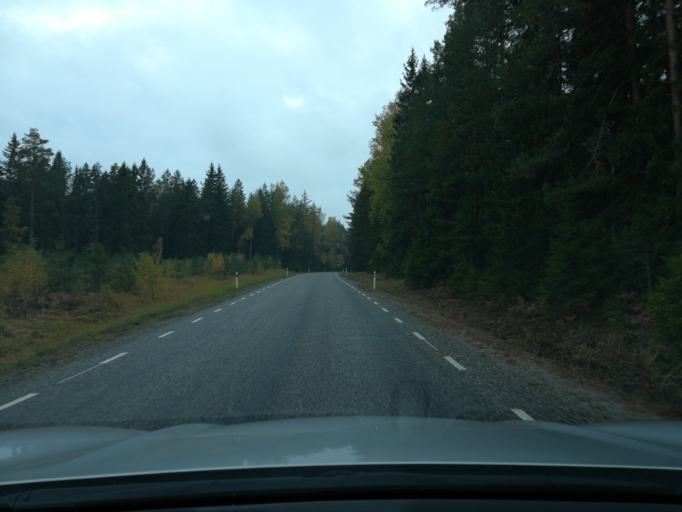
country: EE
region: Ida-Virumaa
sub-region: Johvi vald
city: Johvi
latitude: 59.1680
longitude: 27.4411
